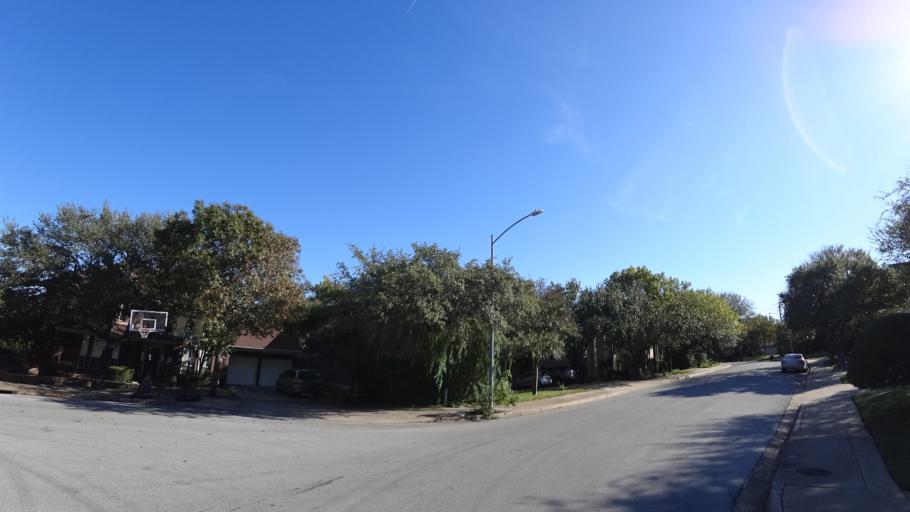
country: US
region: Texas
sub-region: Williamson County
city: Jollyville
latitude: 30.4205
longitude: -97.7778
